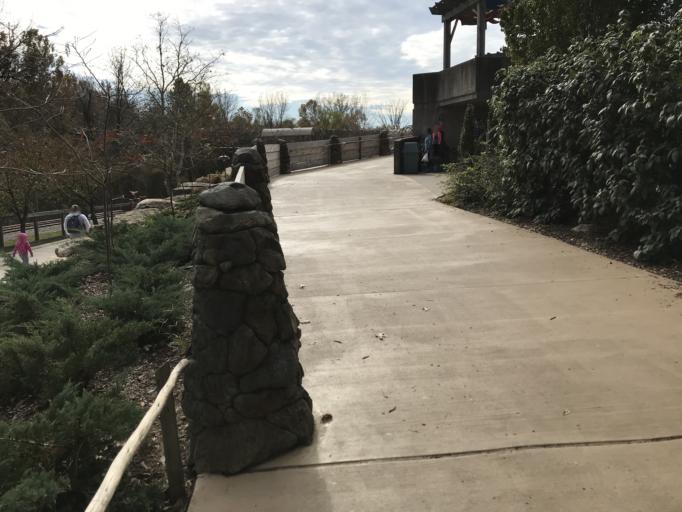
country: US
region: Kentucky
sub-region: Jefferson County
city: Audubon Park
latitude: 38.2063
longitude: -85.7017
